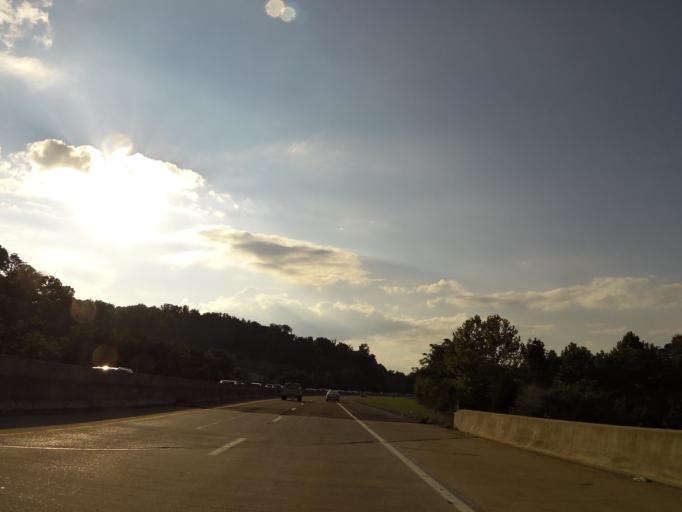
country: US
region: Tennessee
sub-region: Knox County
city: Farragut
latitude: 35.8909
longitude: -84.1118
